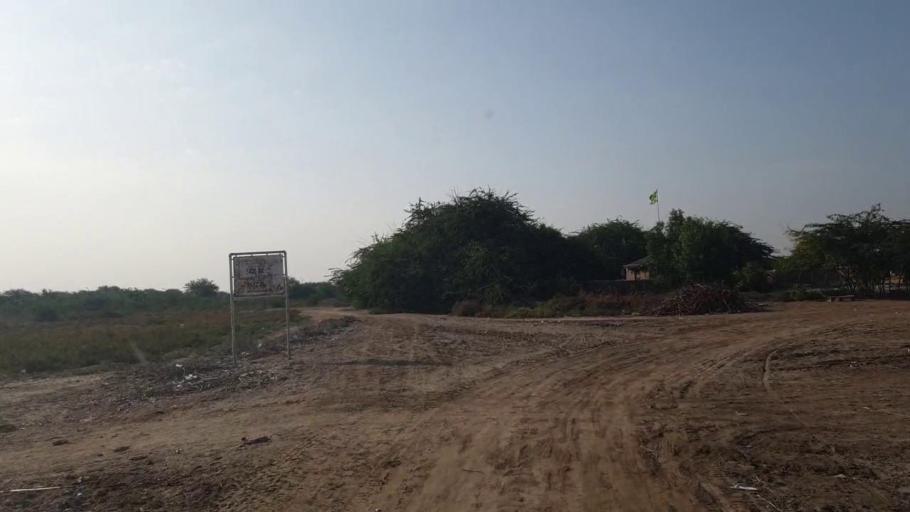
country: PK
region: Sindh
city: Badin
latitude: 24.4522
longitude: 68.7232
